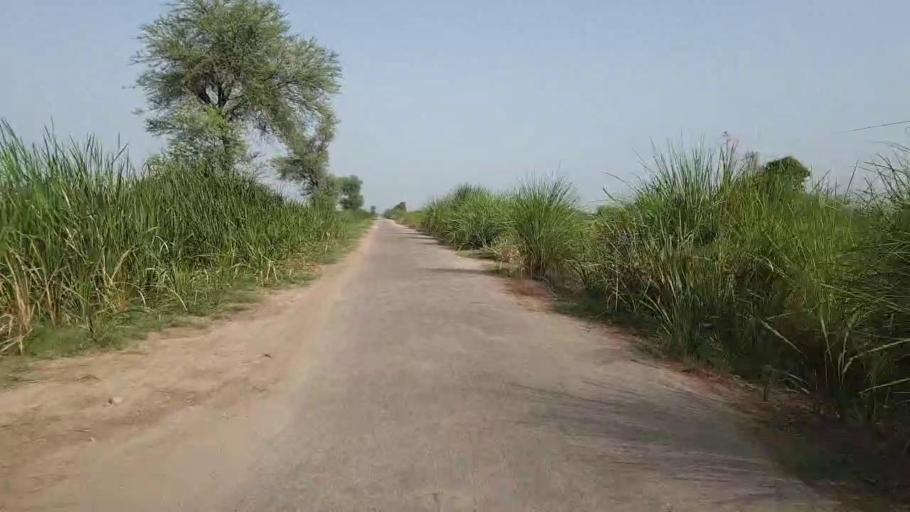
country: PK
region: Sindh
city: Daur
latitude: 26.3492
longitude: 68.1748
